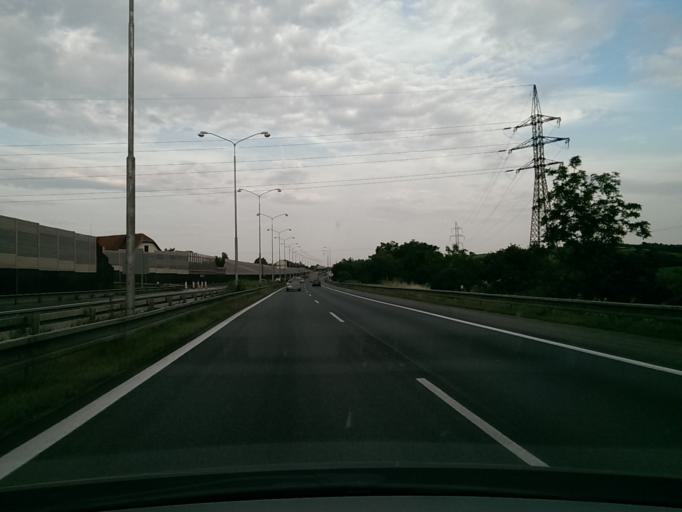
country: CZ
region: South Moravian
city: Ostopovice
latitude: 49.1670
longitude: 16.5463
